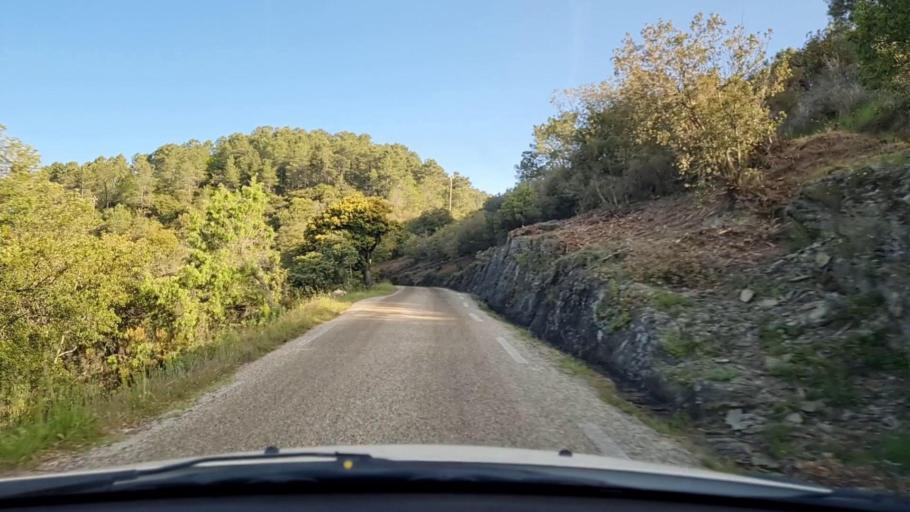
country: FR
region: Languedoc-Roussillon
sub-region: Departement du Gard
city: Branoux-les-Taillades
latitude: 44.1853
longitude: 3.9876
